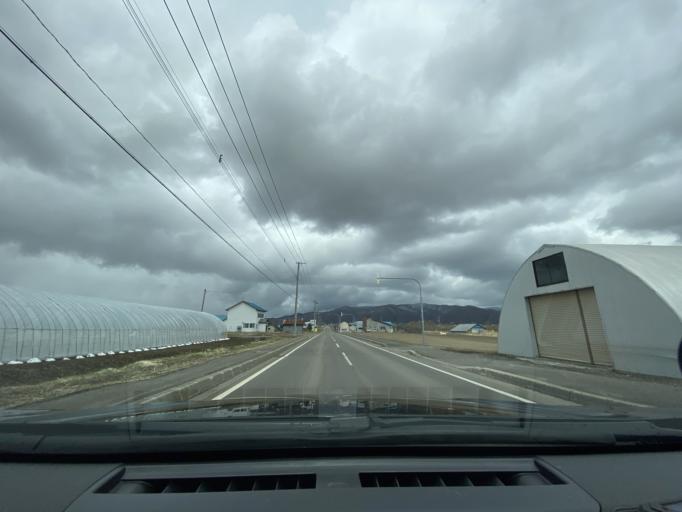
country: JP
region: Hokkaido
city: Nayoro
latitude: 44.1099
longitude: 142.4786
